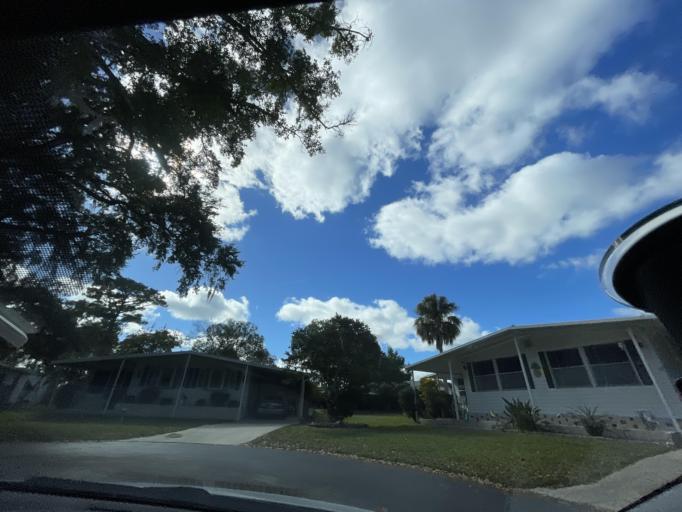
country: US
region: Florida
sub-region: Volusia County
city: South Daytona
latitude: 29.1694
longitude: -81.0328
